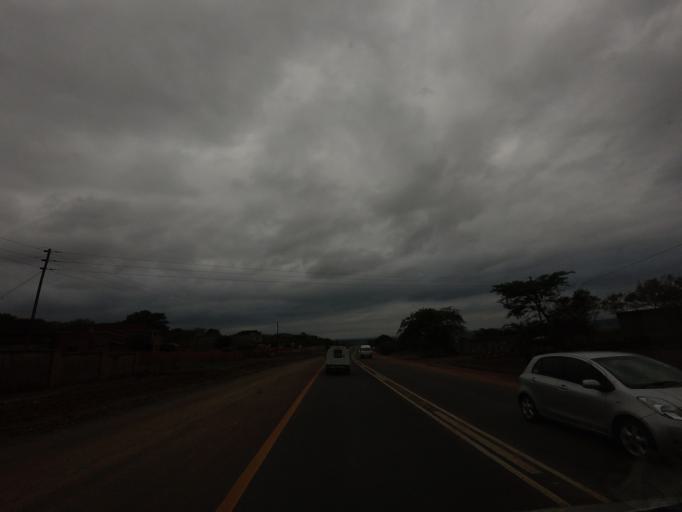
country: SZ
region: Hhohho
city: Ntfonjeni
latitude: -25.6803
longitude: 31.5024
